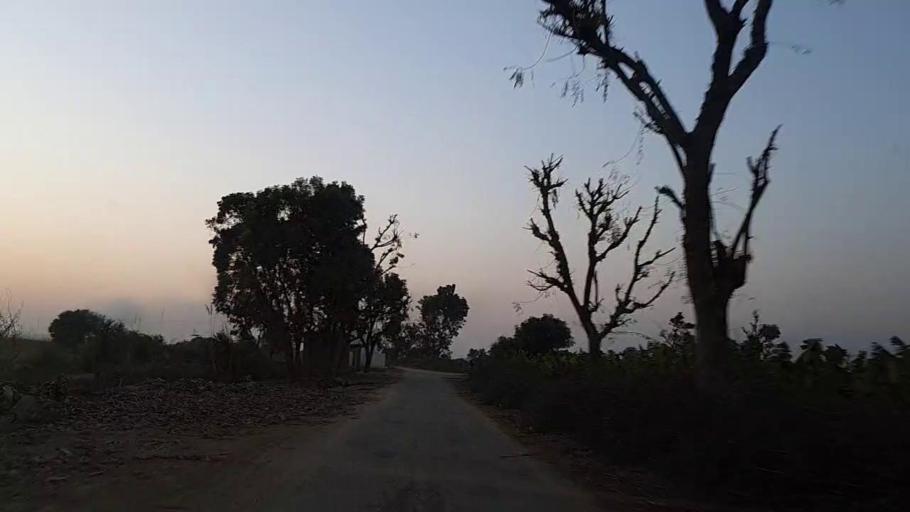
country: PK
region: Sindh
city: Hala
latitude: 25.9573
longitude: 68.4214
